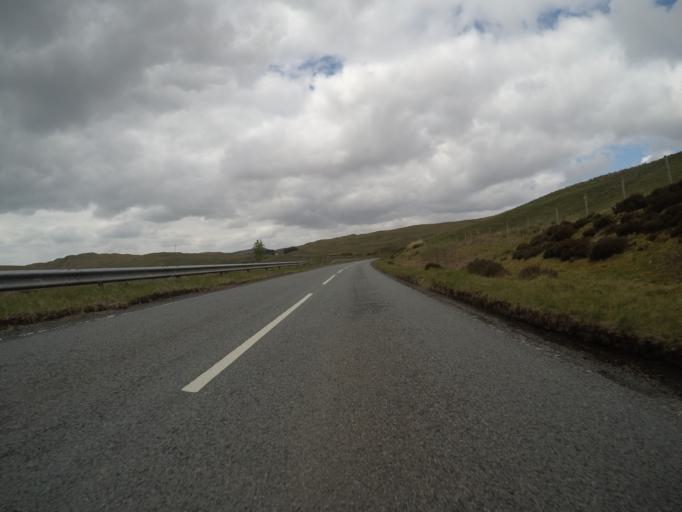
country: GB
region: Scotland
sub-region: Highland
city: Isle of Skye
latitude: 57.3250
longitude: -6.3322
